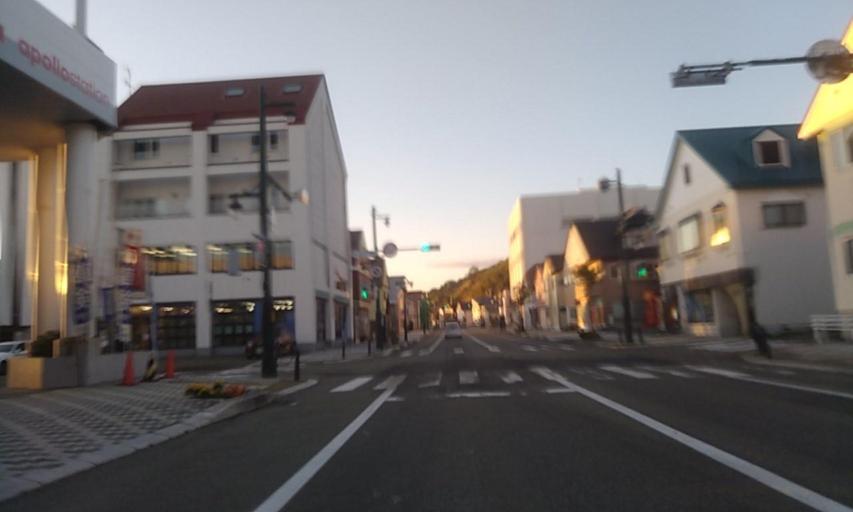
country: JP
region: Hokkaido
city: Shizunai-furukawacho
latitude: 42.1626
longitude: 142.7747
